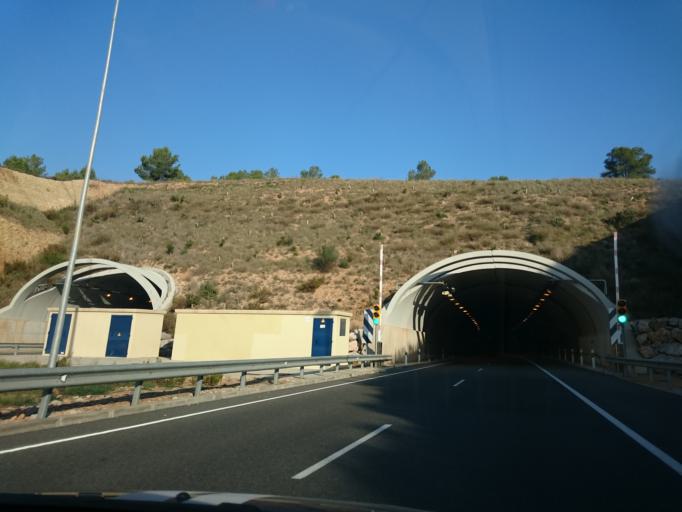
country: ES
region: Catalonia
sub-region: Provincia de Barcelona
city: Sant Pere de Ribes
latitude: 41.2817
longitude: 1.7292
